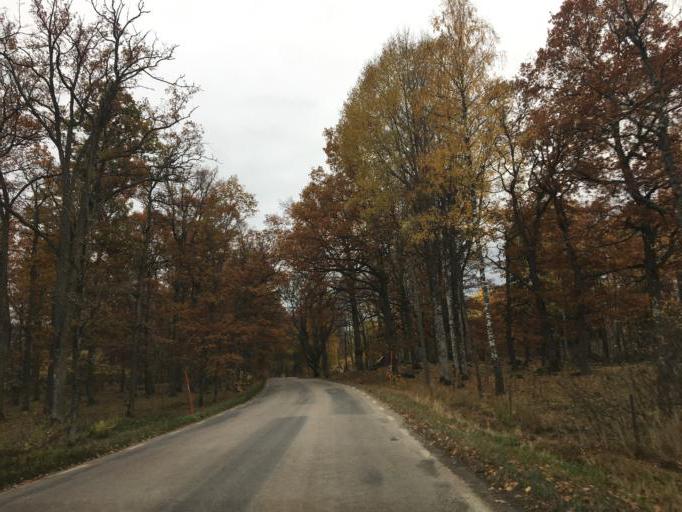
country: SE
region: Vaestmanland
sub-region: Hallstahammars Kommun
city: Kolback
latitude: 59.5275
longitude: 16.2864
